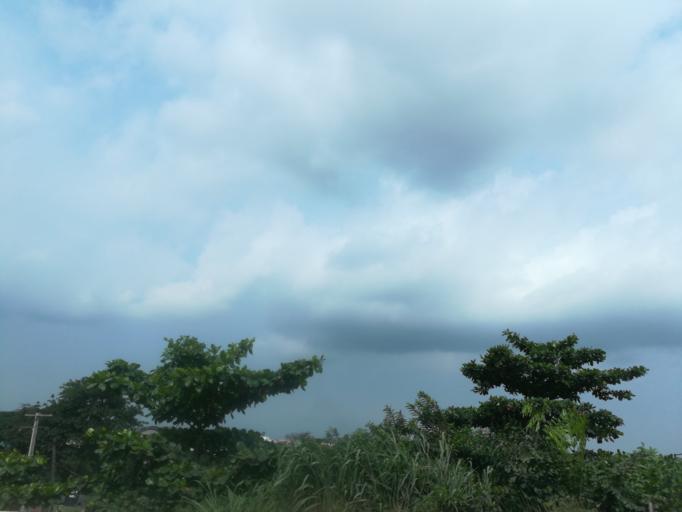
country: NG
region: Lagos
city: Ikeja
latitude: 6.6221
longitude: 3.3642
